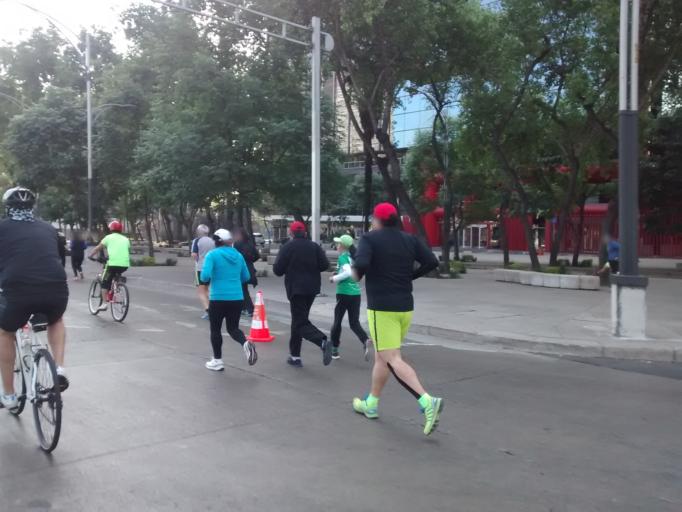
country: MX
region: Mexico City
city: Cuauhtemoc
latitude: 19.4307
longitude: -99.1597
